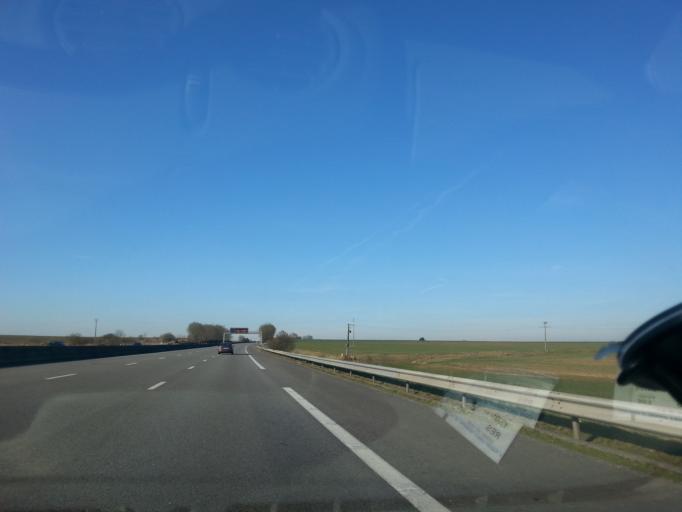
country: FR
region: Haute-Normandie
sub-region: Departement de l'Eure
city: Ande
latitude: 49.1674
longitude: 1.2546
